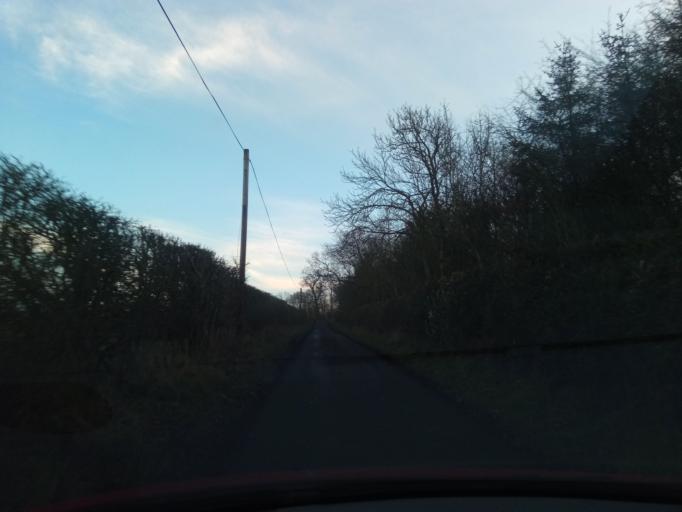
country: GB
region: Scotland
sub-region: The Scottish Borders
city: Saint Boswells
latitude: 55.5252
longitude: -2.6597
